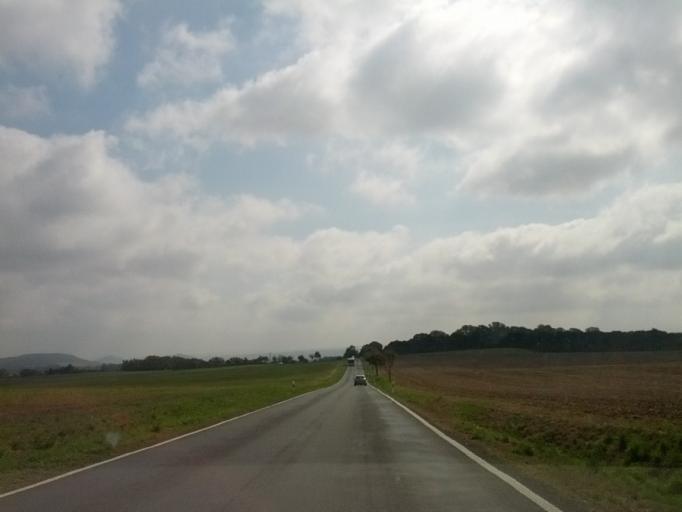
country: DE
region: Thuringia
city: Schwabhausen
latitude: 50.9101
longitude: 10.7523
